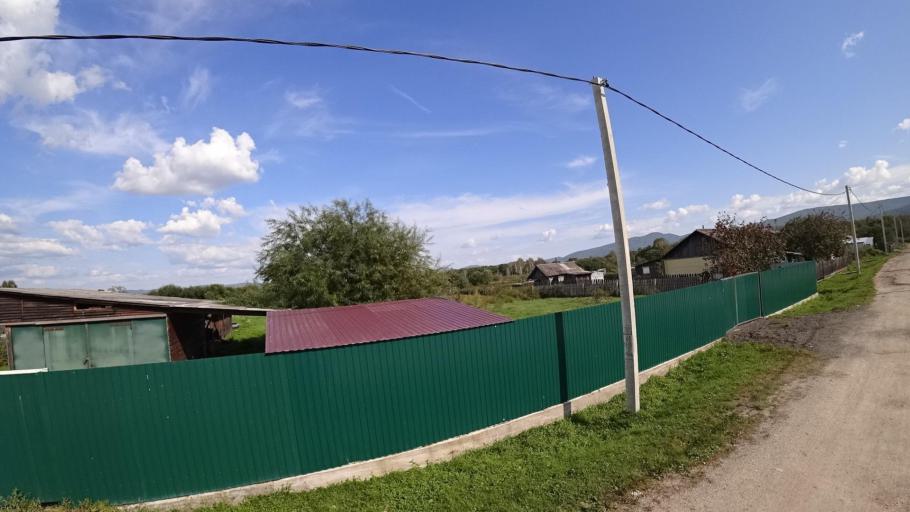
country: RU
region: Jewish Autonomous Oblast
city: Birakan
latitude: 48.9847
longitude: 131.7272
